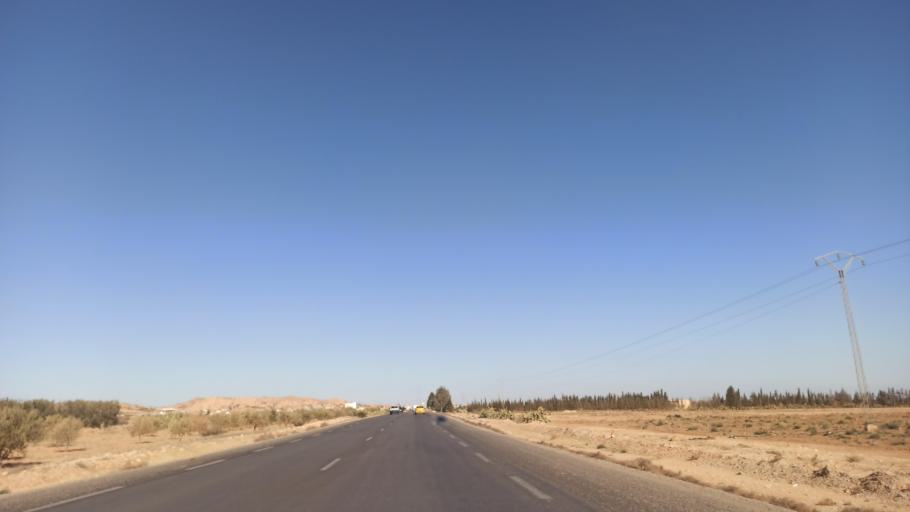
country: TN
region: Sidi Bu Zayd
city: Bi'r al Hufayy
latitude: 34.9053
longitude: 9.1779
